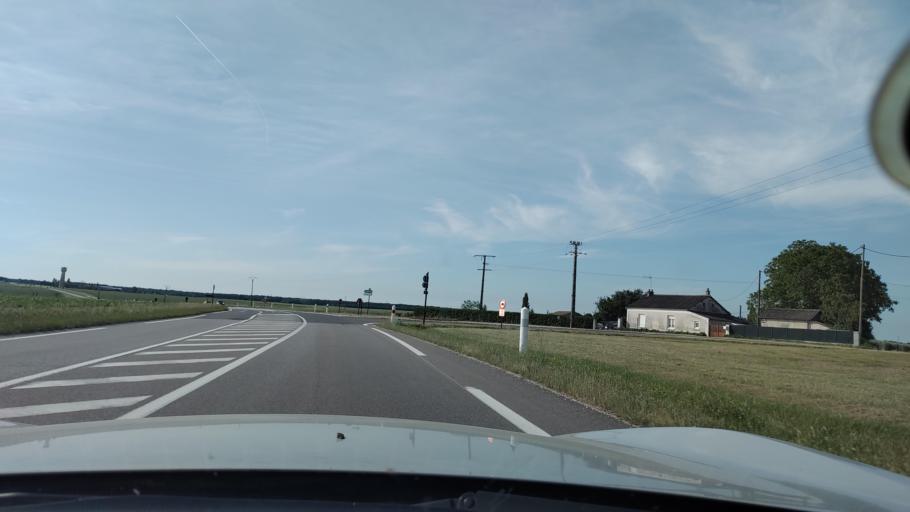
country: FR
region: Ile-de-France
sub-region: Departement de Seine-et-Marne
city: Jouy-le-Chatel
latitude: 48.6625
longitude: 3.1392
